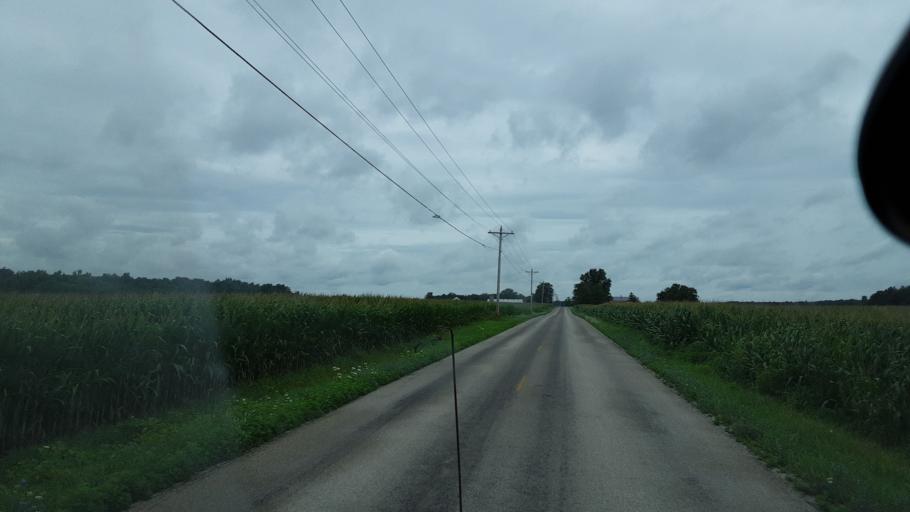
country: US
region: Indiana
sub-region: Jay County
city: Portland
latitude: 40.4706
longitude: -85.0204
